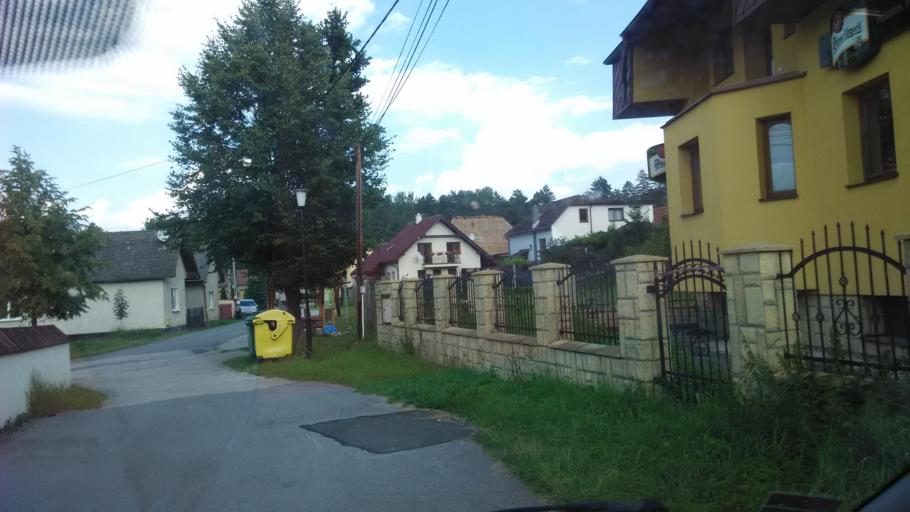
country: SK
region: Zilinsky
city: Kysucke Nove Mesto
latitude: 49.2952
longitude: 18.7884
